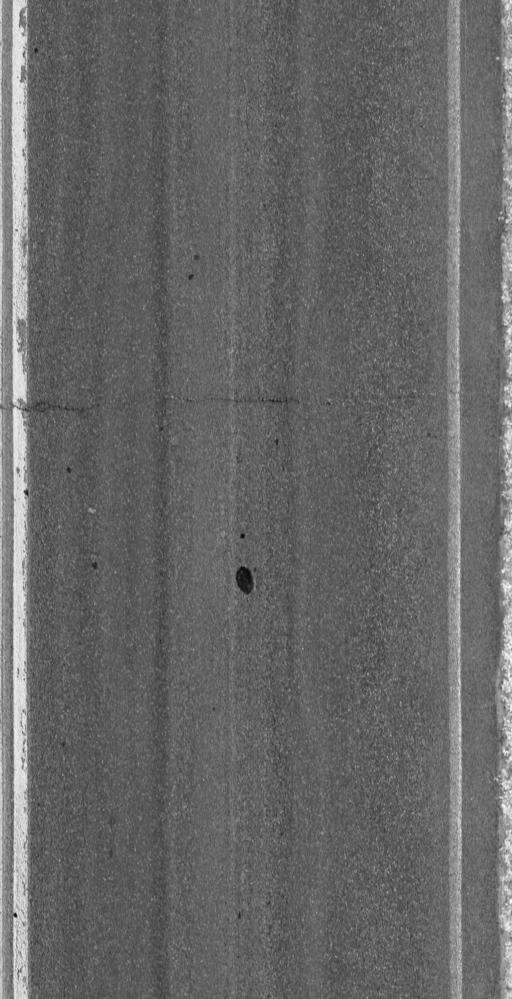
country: US
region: Vermont
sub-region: Chittenden County
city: Essex Junction
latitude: 44.4487
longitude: -73.1267
